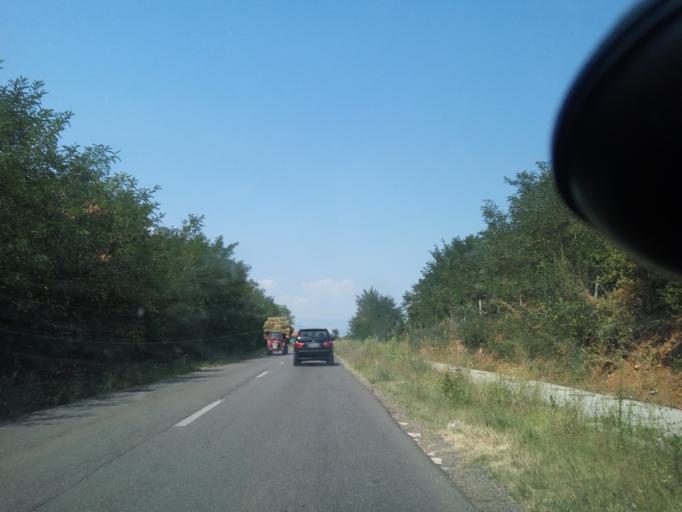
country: XK
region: Gjakova
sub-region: Komuna e Decanit
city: Gllogjan
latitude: 42.4661
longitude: 20.3467
